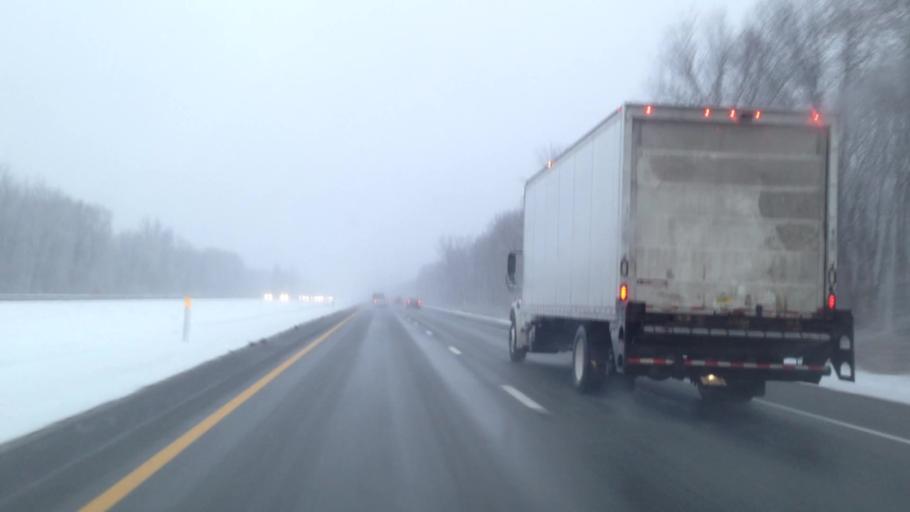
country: US
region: New York
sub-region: Madison County
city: Bolivar
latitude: 43.0916
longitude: -75.9391
